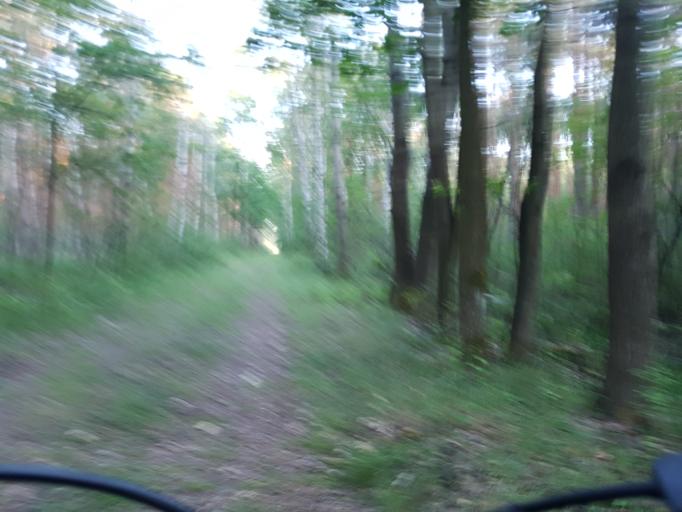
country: DE
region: Brandenburg
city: Schilda
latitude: 51.5882
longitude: 13.3452
